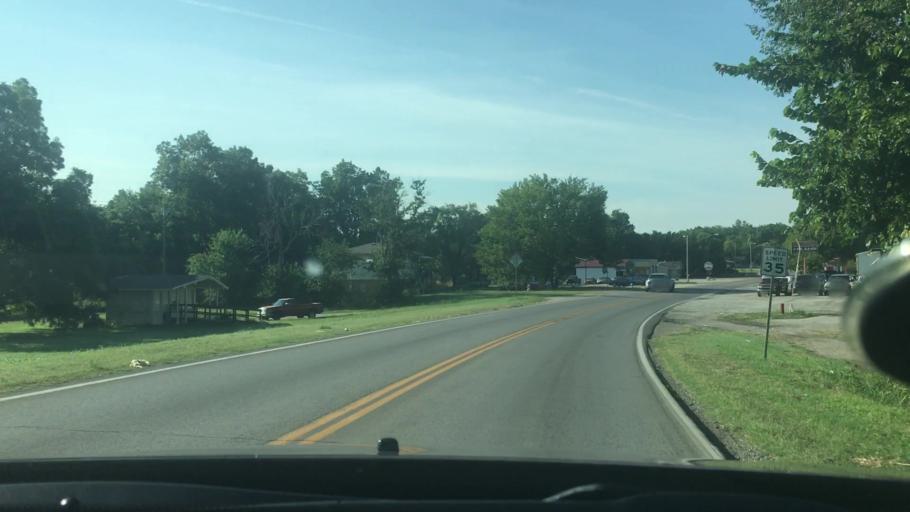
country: US
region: Oklahoma
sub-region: Garvin County
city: Pauls Valley
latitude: 34.7328
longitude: -97.2133
